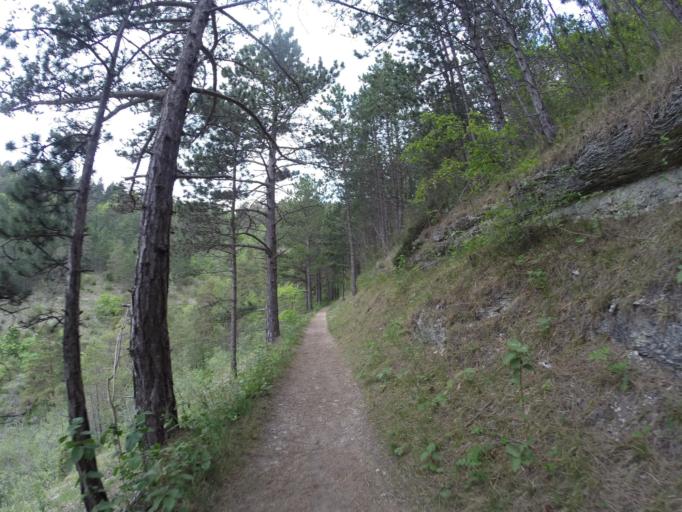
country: DE
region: Thuringia
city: Jena
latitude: 50.9103
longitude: 11.6169
